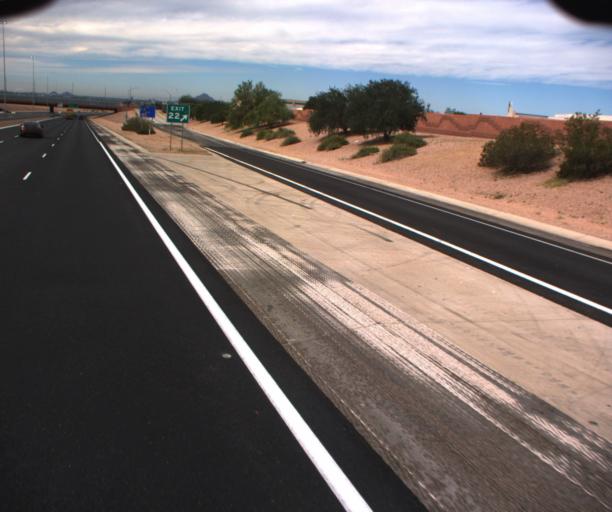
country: US
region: Arizona
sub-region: Maricopa County
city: Mesa
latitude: 33.4755
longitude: -111.6971
